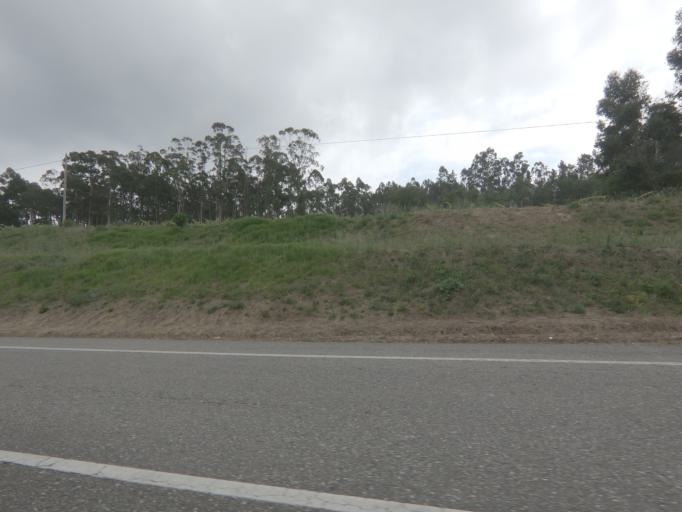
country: ES
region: Galicia
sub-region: Provincia de Pontevedra
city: O Rosal
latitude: 41.9327
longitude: -8.7947
